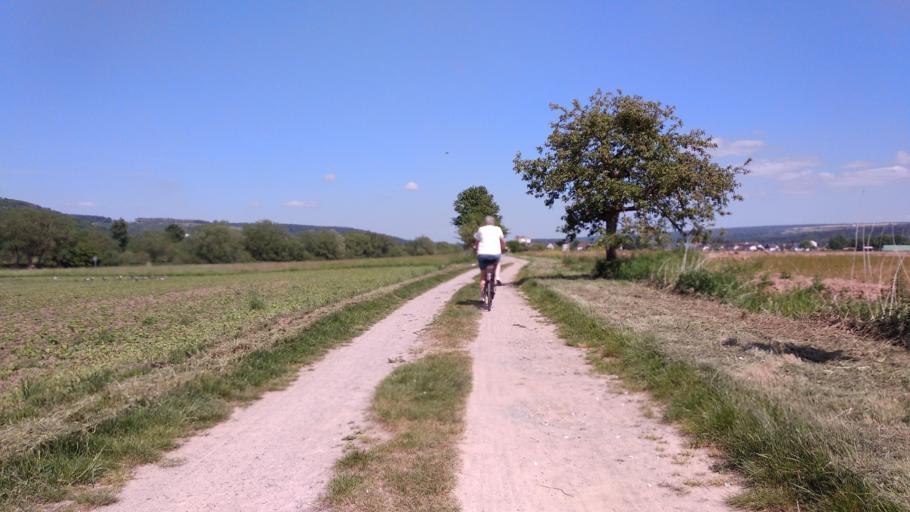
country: DE
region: North Rhine-Westphalia
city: Beverungen
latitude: 51.6521
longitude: 9.3770
